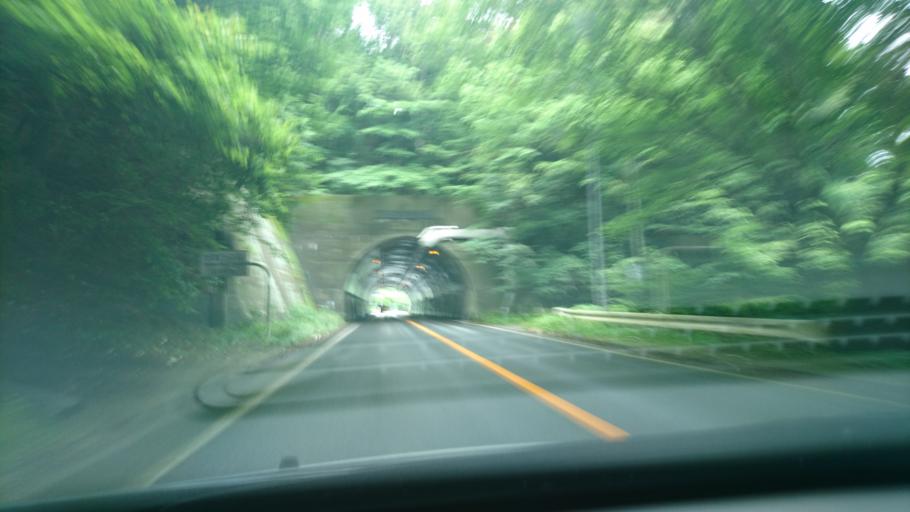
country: JP
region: Iwate
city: Otsuchi
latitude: 39.3987
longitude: 141.9503
